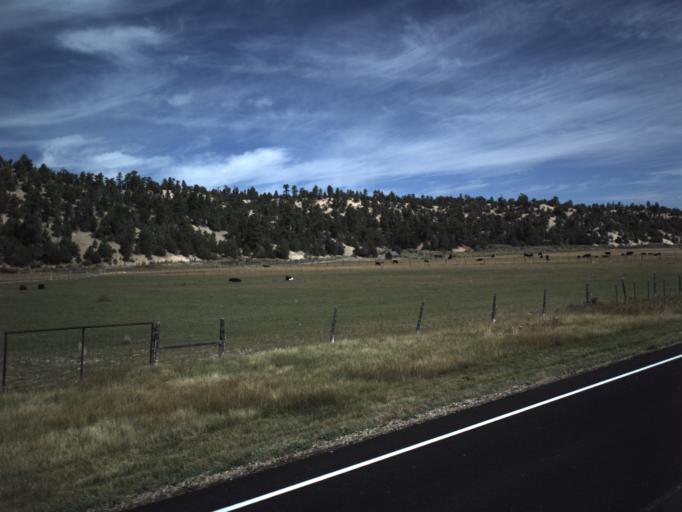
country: US
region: Utah
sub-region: Garfield County
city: Panguitch
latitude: 37.6859
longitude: -111.8087
